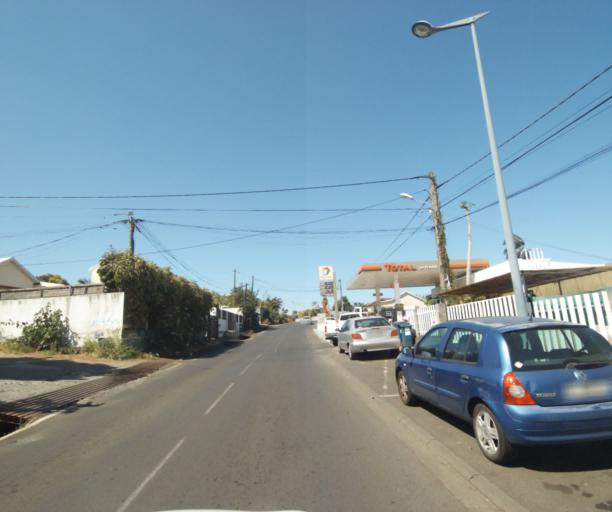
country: RE
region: Reunion
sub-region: Reunion
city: La Possession
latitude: -20.9782
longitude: 55.3289
